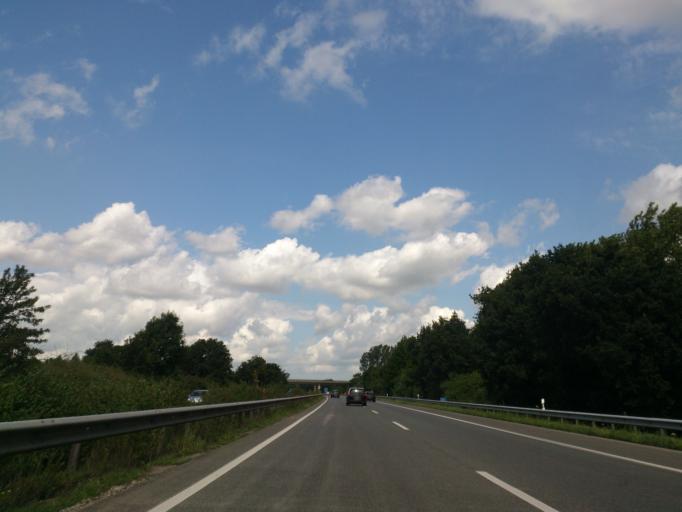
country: DE
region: Schleswig-Holstein
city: Klein Offenseth-Sparrieshoop
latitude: 53.7927
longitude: 9.6967
